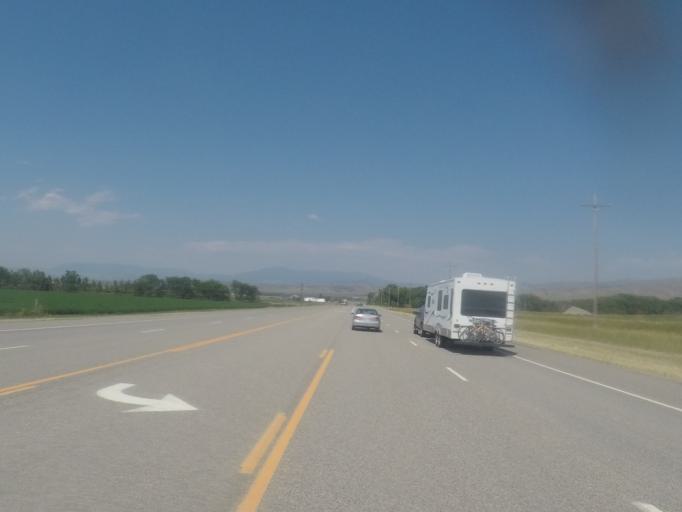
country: US
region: Montana
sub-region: Broadwater County
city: Townsend
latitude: 46.1493
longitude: -111.4689
